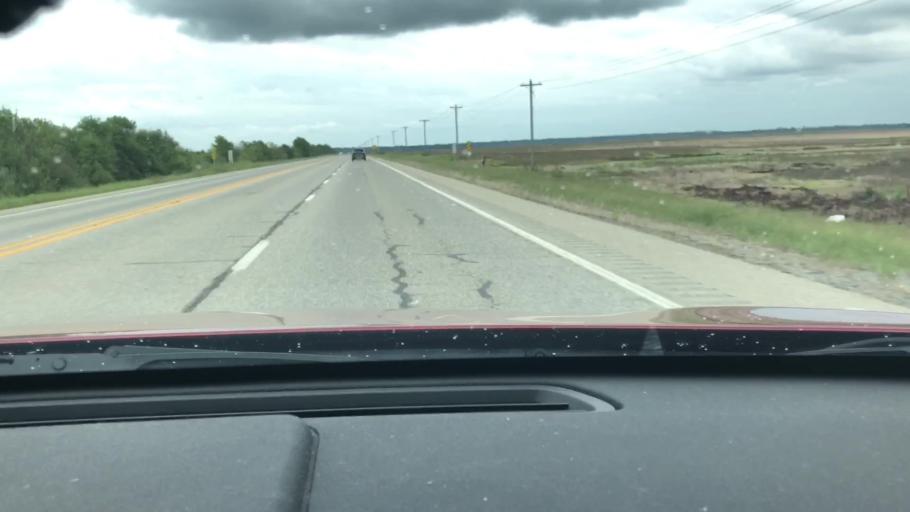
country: US
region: Arkansas
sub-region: Lafayette County
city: Lewisville
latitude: 33.4122
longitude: -93.7858
